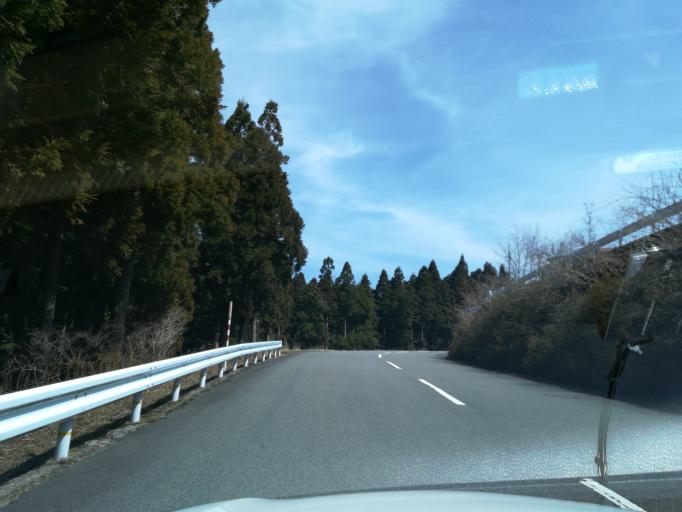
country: JP
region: Tokushima
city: Wakimachi
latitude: 33.8779
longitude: 134.0569
